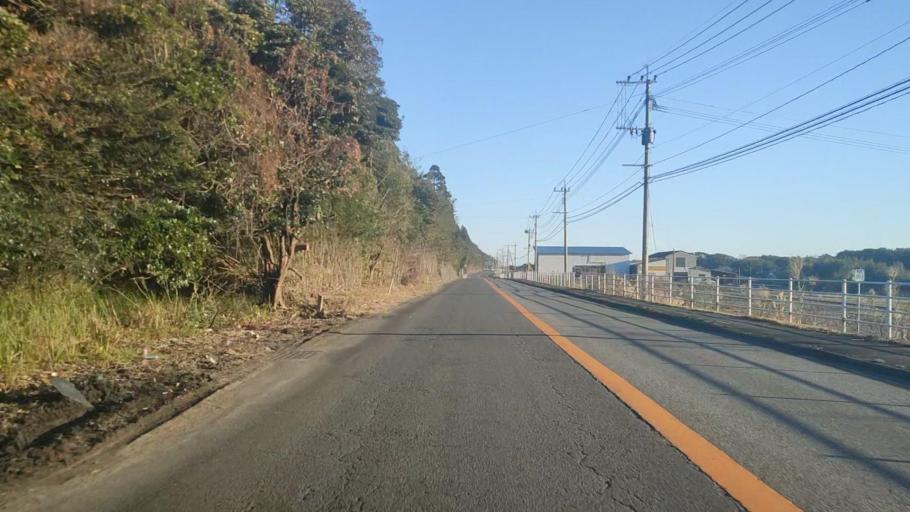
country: JP
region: Miyazaki
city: Takanabe
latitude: 32.0977
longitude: 131.5185
